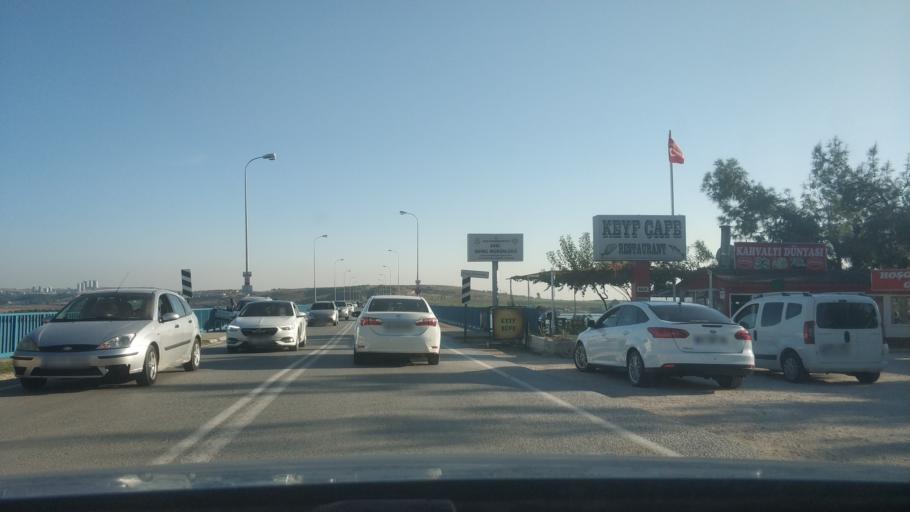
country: TR
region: Adana
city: Adana
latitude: 37.1042
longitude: 35.2991
